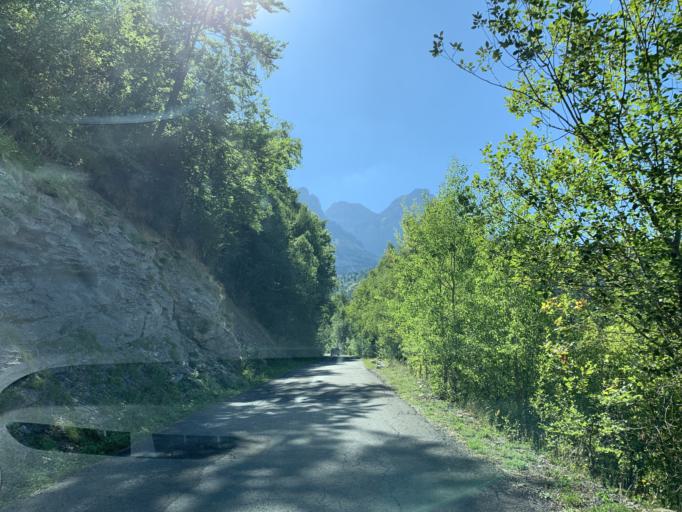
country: ES
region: Aragon
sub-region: Provincia de Huesca
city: Hoz de Jaca
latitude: 42.6925
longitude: -0.3241
